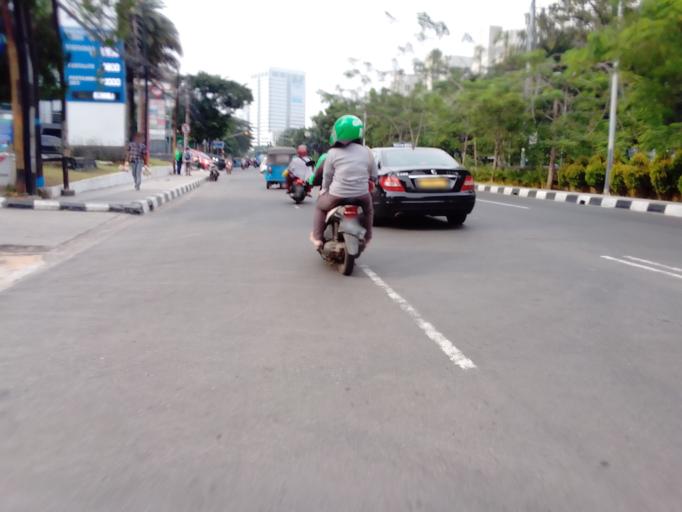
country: ID
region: Jakarta Raya
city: Jakarta
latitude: -6.1789
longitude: 106.8185
